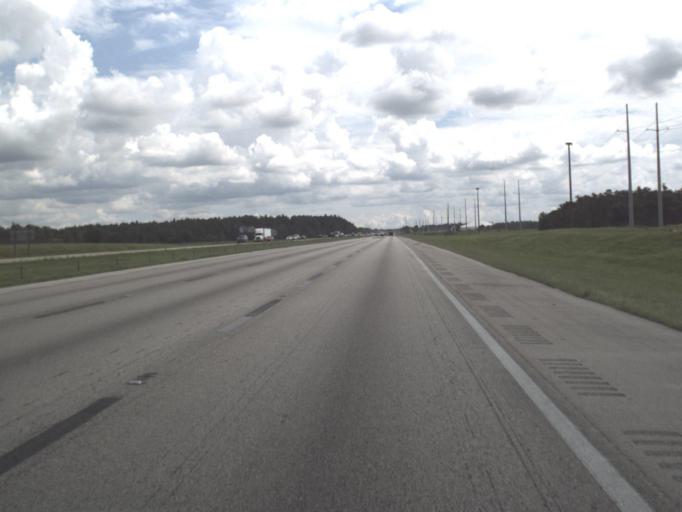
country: US
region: Florida
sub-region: Polk County
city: Polk City
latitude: 28.1455
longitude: -81.8785
